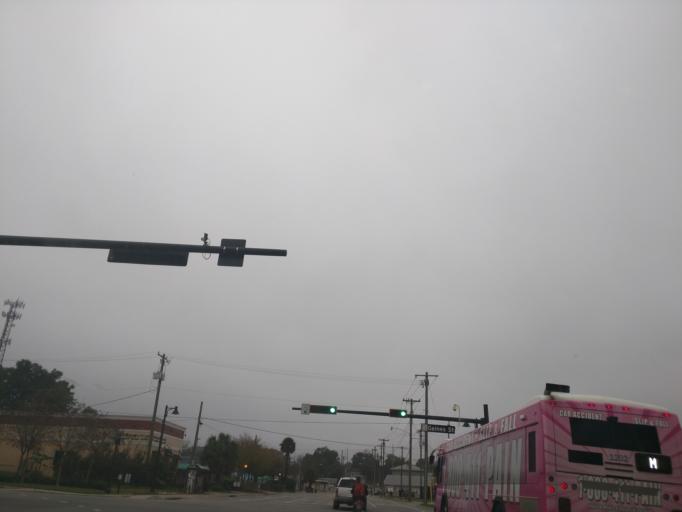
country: US
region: Florida
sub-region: Leon County
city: Tallahassee
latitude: 30.4358
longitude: -84.2897
